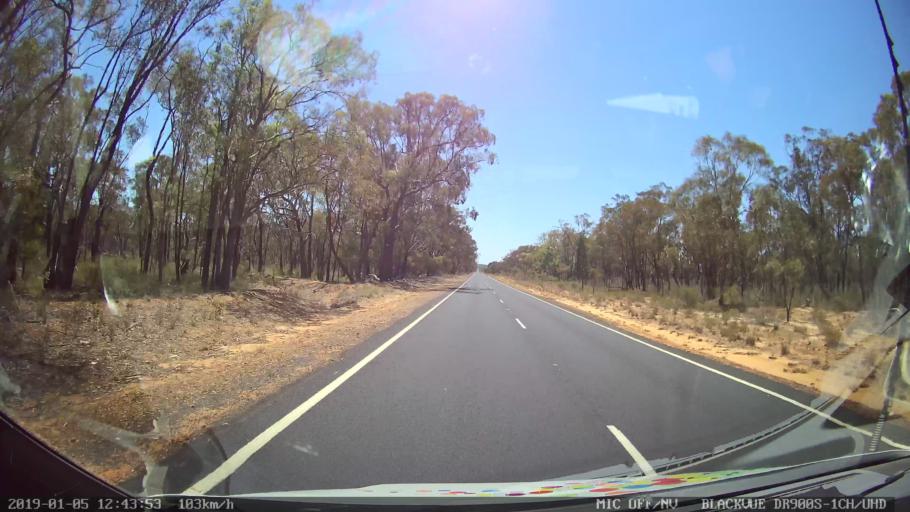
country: AU
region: New South Wales
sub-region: Warrumbungle Shire
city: Coonabarabran
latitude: -31.1434
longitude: 149.5301
